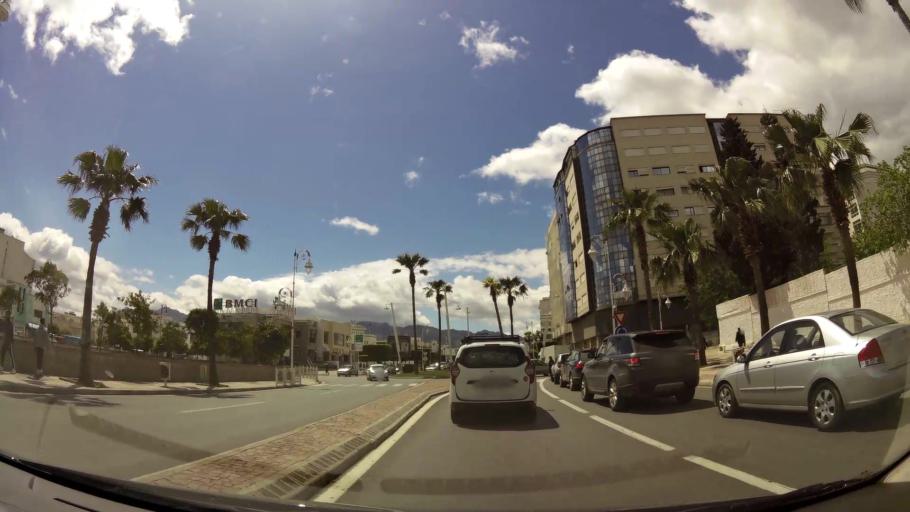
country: MA
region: Tanger-Tetouan
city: Tetouan
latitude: 35.5862
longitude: -5.3476
